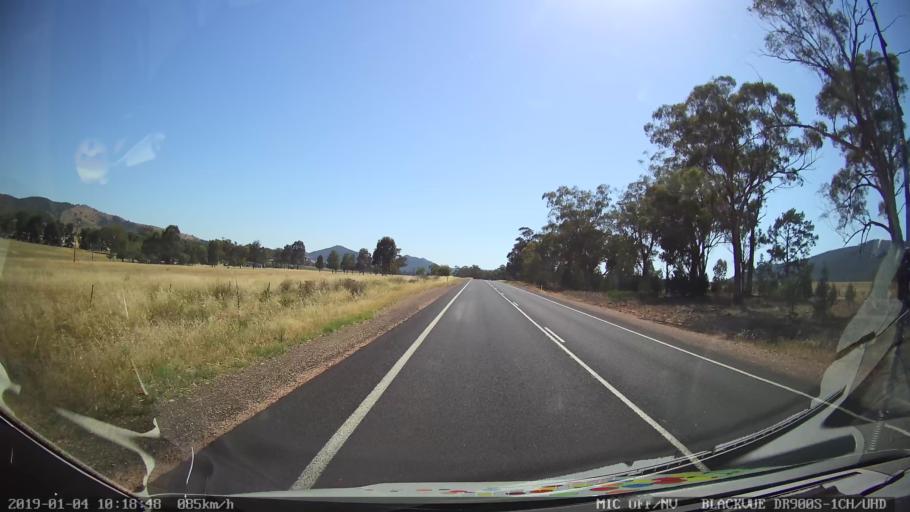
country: AU
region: New South Wales
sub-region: Cabonne
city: Canowindra
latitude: -33.3802
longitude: 148.4716
